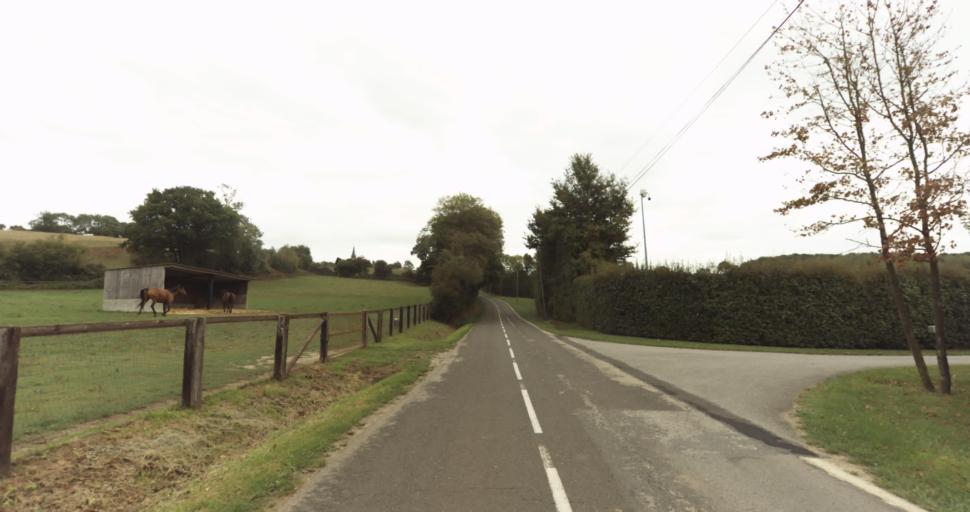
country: FR
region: Lower Normandy
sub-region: Departement de l'Orne
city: Gace
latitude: 48.7112
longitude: 0.3254
